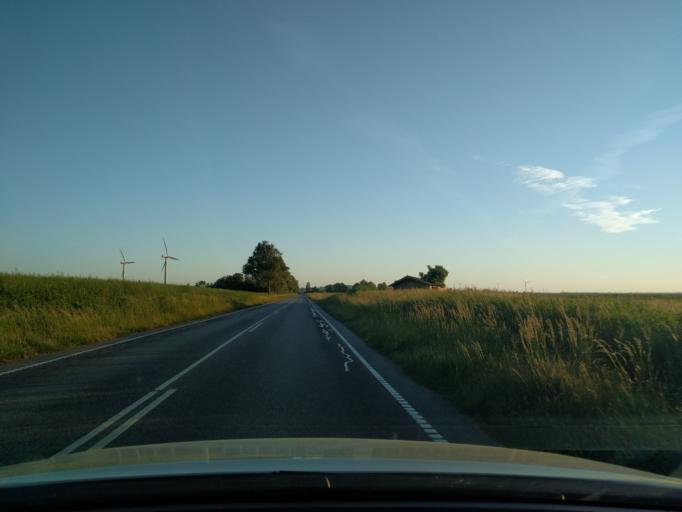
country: DK
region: South Denmark
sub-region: Kerteminde Kommune
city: Kerteminde
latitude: 55.4891
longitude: 10.6330
